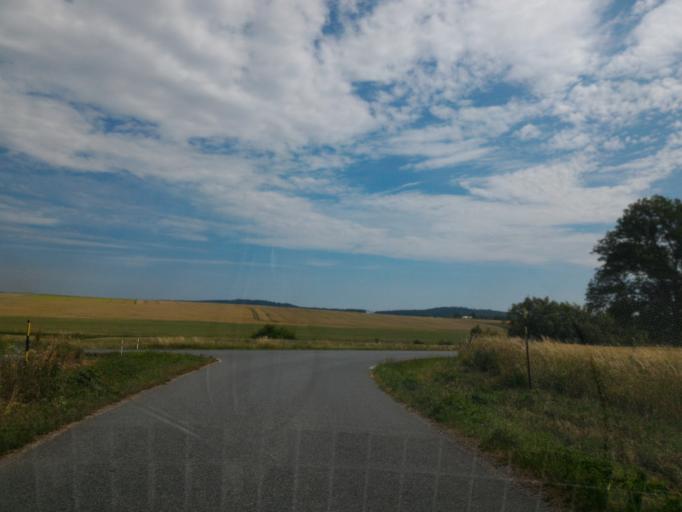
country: CZ
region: Vysocina
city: Nove Syrovice
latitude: 49.0694
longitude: 15.7520
